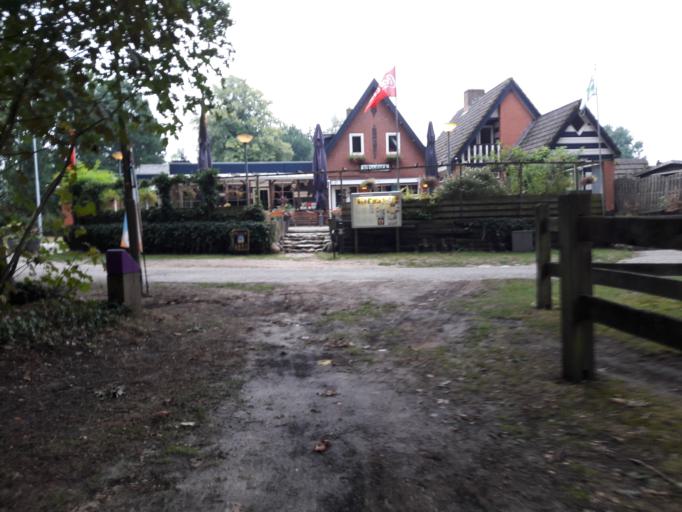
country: NL
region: Drenthe
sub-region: Gemeente Borger-Odoorn
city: Borger
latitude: 52.9568
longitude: 6.7979
